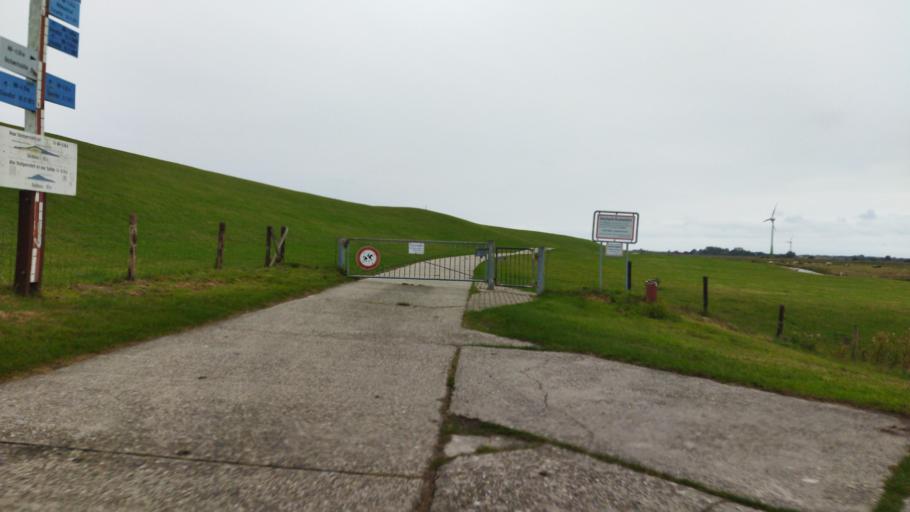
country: DE
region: Lower Saxony
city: Hinte
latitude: 53.4860
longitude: 7.0318
